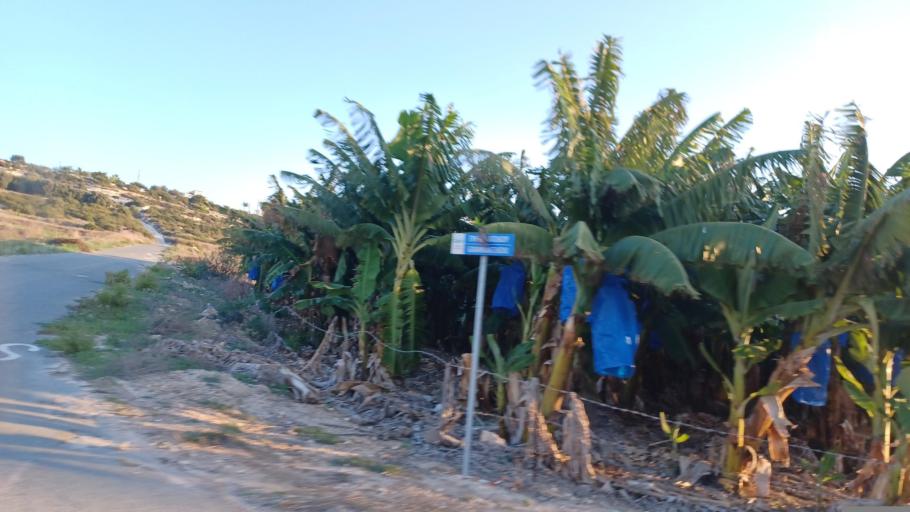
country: CY
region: Pafos
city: Pegeia
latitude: 34.8690
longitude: 32.3518
